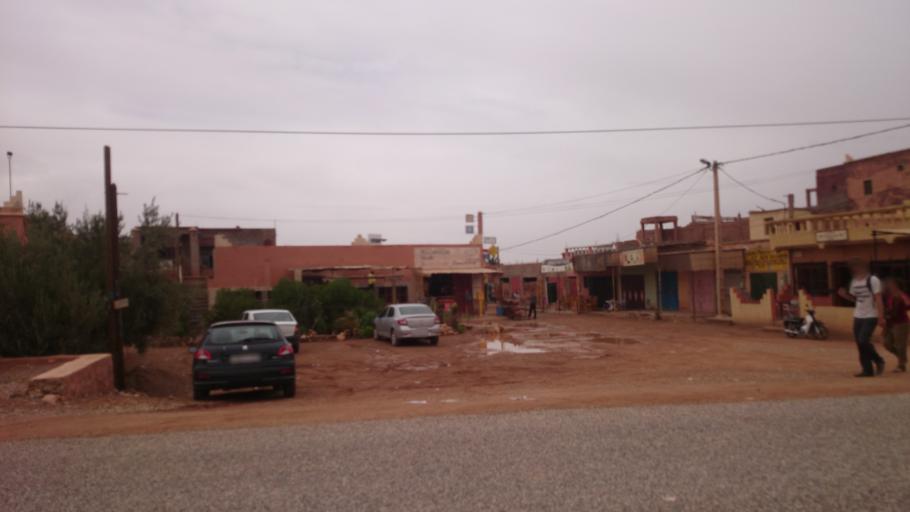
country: MA
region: Souss-Massa-Draa
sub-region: Ouarzazate
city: Amerzgane
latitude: 31.0441
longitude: -7.1320
